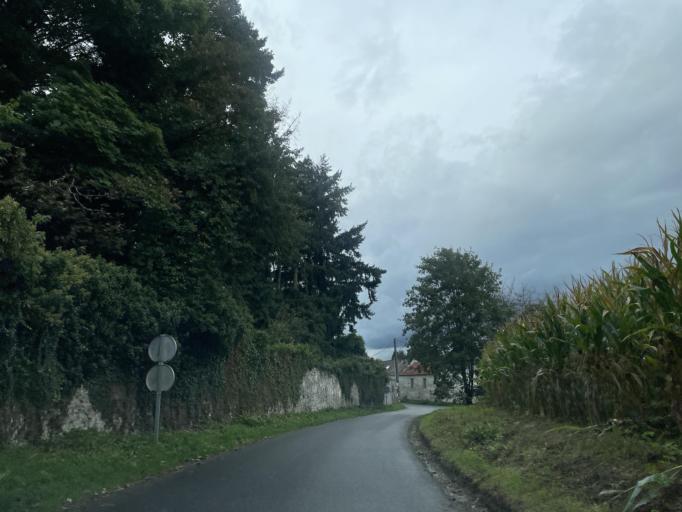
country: FR
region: Ile-de-France
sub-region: Departement de Seine-et-Marne
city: Trilport
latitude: 48.9375
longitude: 2.9654
